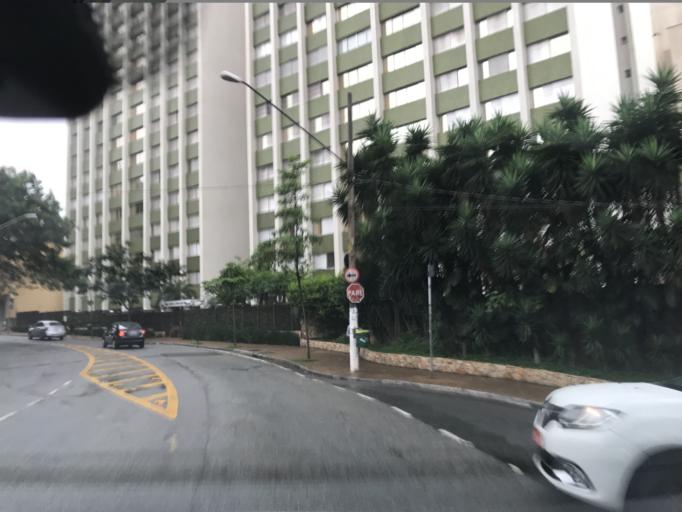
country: BR
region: Sao Paulo
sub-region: Sao Paulo
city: Sao Paulo
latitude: -23.5383
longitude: -46.6836
